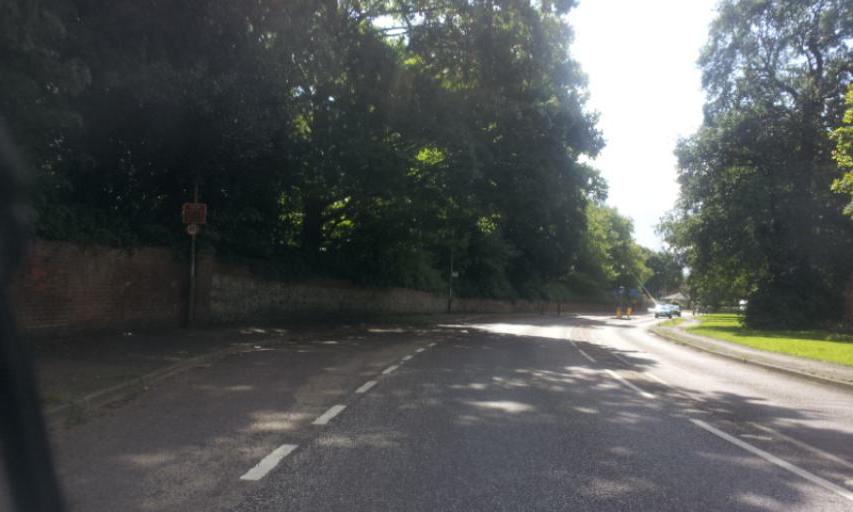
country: GB
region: England
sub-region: Kent
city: Larkfield
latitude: 51.2946
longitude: 0.4385
